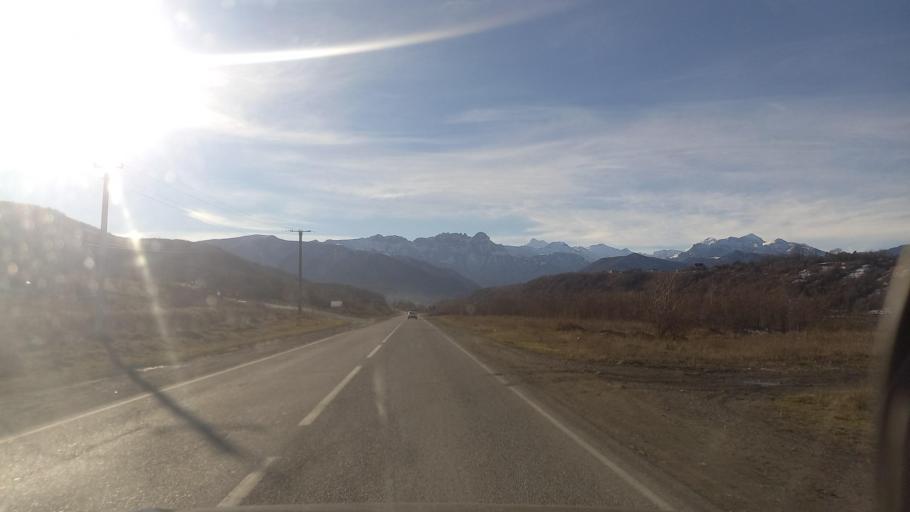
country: RU
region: North Ossetia
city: Gizel'
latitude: 43.0127
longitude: 44.5696
